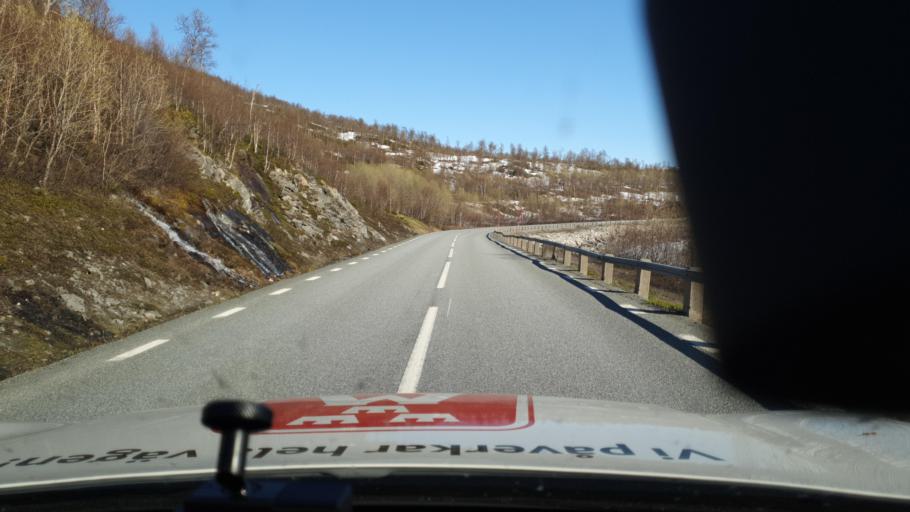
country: NO
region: Nordland
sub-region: Rana
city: Mo i Rana
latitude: 66.1089
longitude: 14.8180
